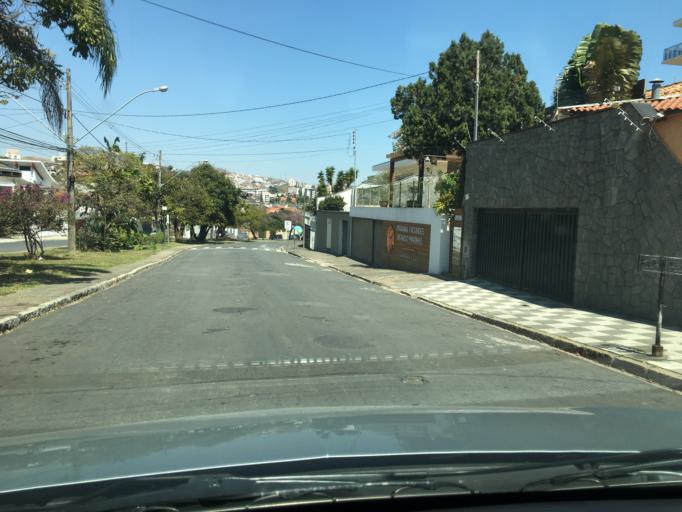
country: BR
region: Minas Gerais
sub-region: Pocos De Caldas
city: Pocos de Caldas
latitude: -21.7817
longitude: -46.5599
